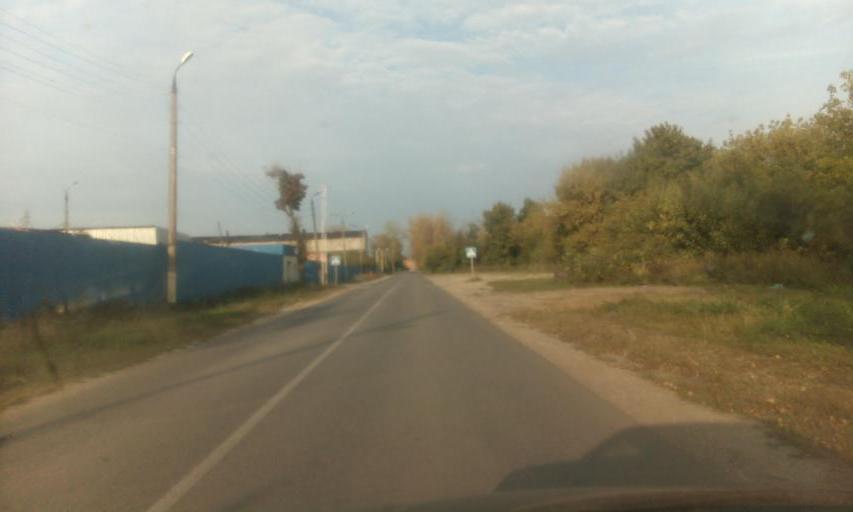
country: RU
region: Tula
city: Partizan
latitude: 53.9269
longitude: 38.1189
